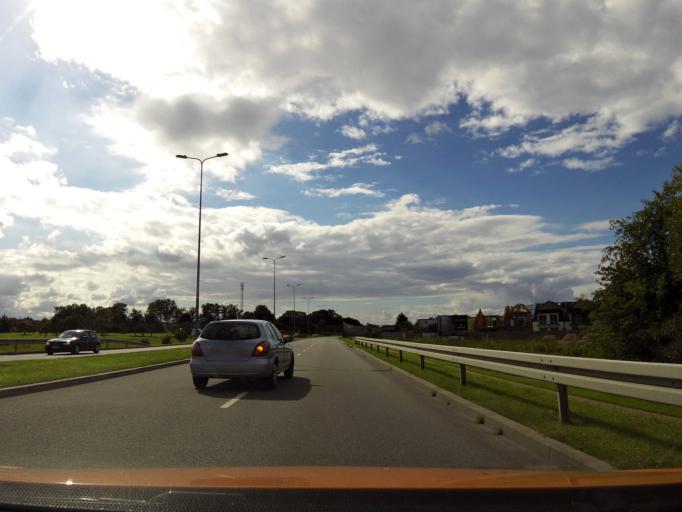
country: PL
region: West Pomeranian Voivodeship
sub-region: Powiat kolobrzeski
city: Kolobrzeg
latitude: 54.1629
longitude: 15.5591
